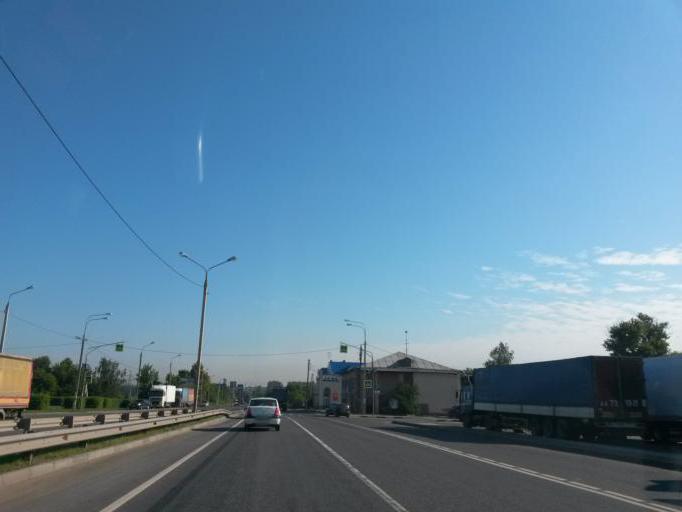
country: RU
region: Moskovskaya
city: Yam
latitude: 55.4887
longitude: 37.7502
